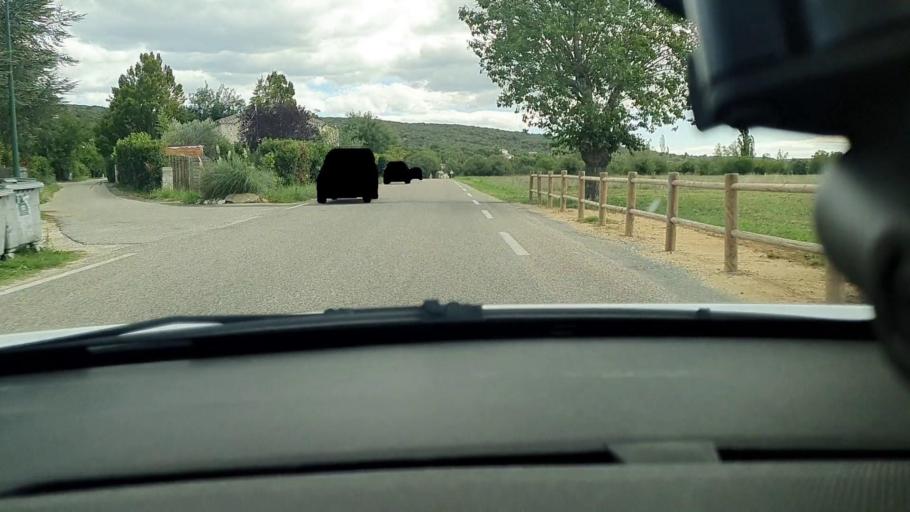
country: FR
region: Languedoc-Roussillon
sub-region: Departement du Gard
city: Salindres
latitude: 44.1792
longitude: 4.2366
